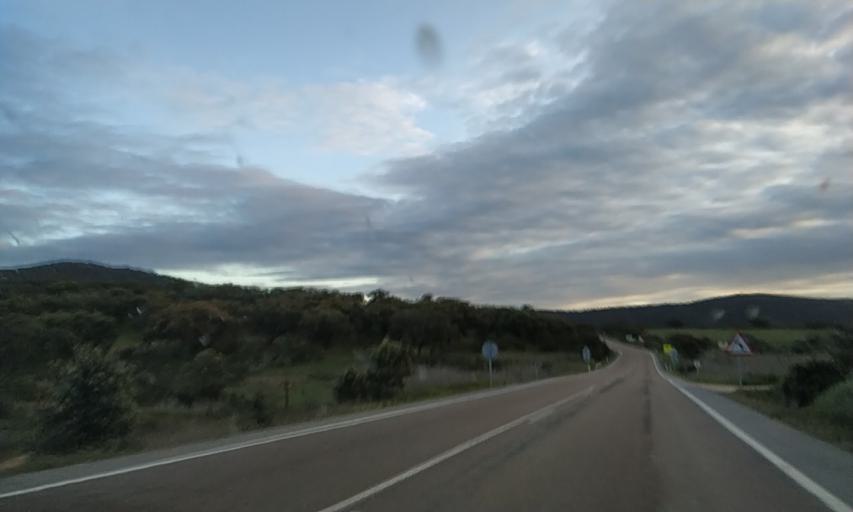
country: ES
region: Extremadura
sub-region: Provincia de Caceres
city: Malpartida de Caceres
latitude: 39.3002
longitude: -6.5166
